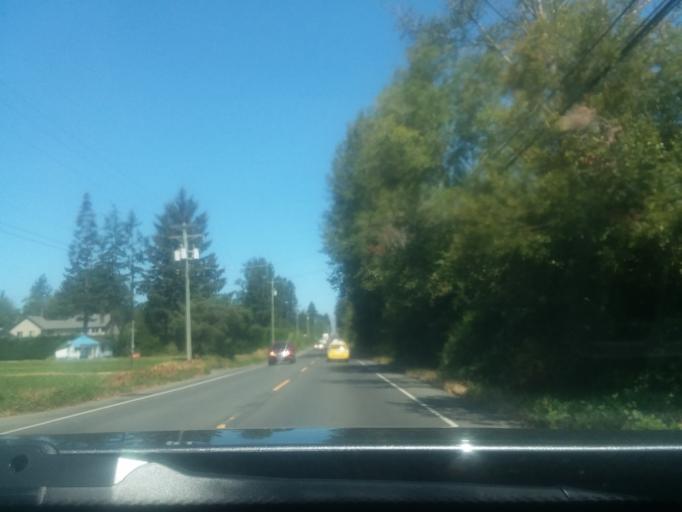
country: CA
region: British Columbia
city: Courtenay
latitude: 49.6929
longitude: -124.9346
